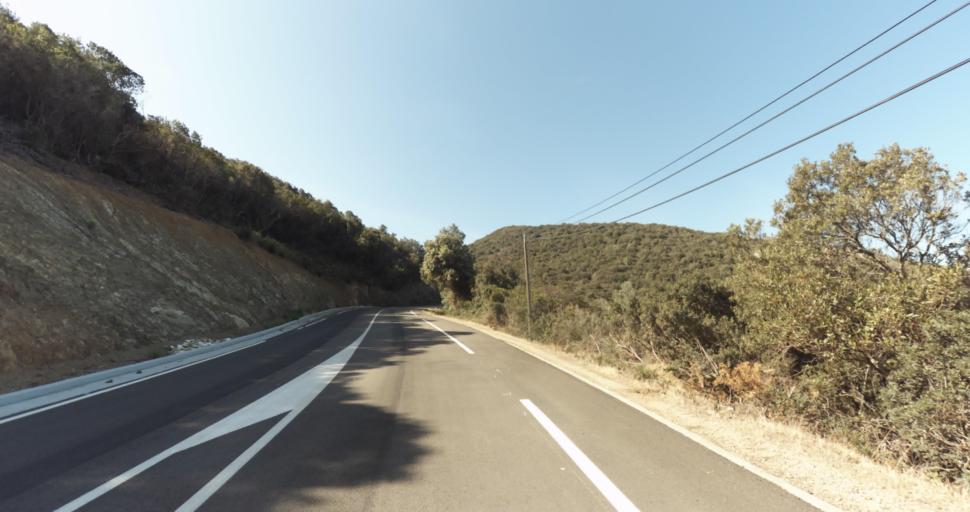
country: FR
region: Corsica
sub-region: Departement de la Corse-du-Sud
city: Ajaccio
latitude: 41.9247
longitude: 8.6433
